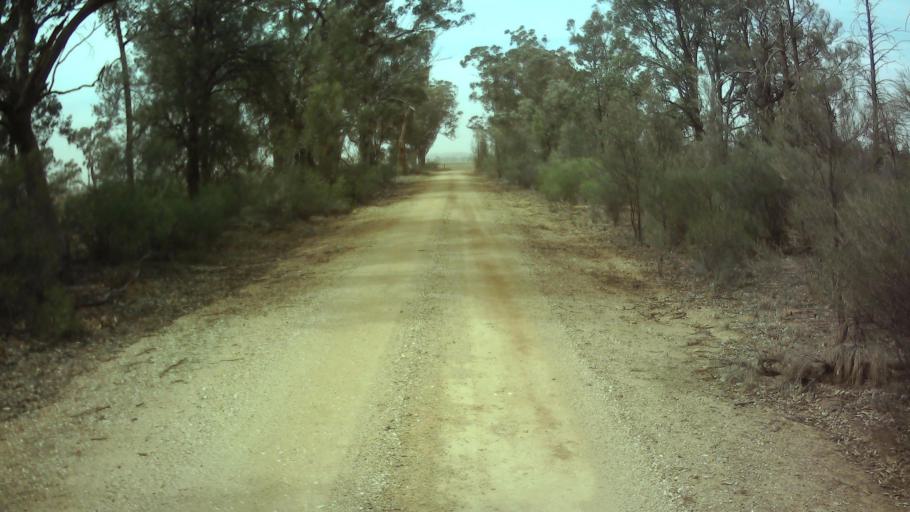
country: AU
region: New South Wales
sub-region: Weddin
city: Grenfell
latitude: -33.7165
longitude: 147.9694
